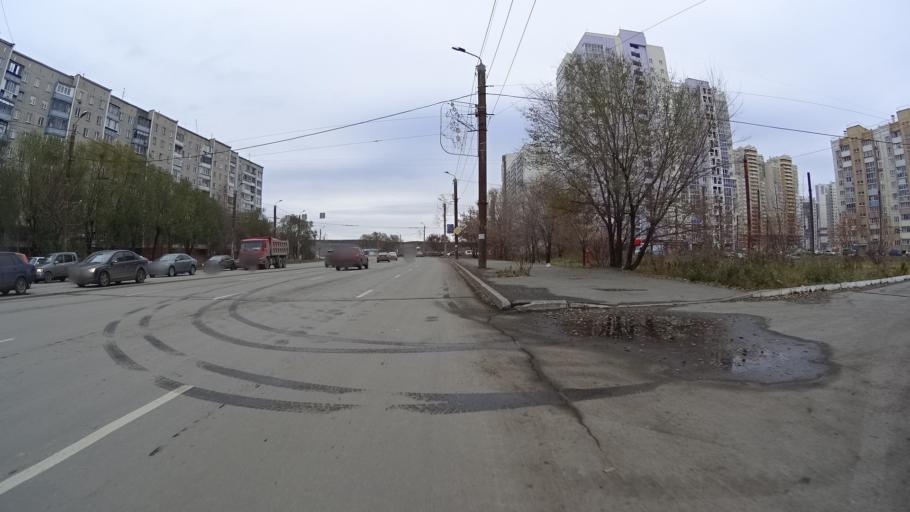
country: RU
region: Chelyabinsk
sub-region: Gorod Chelyabinsk
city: Chelyabinsk
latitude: 55.1780
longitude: 61.3326
